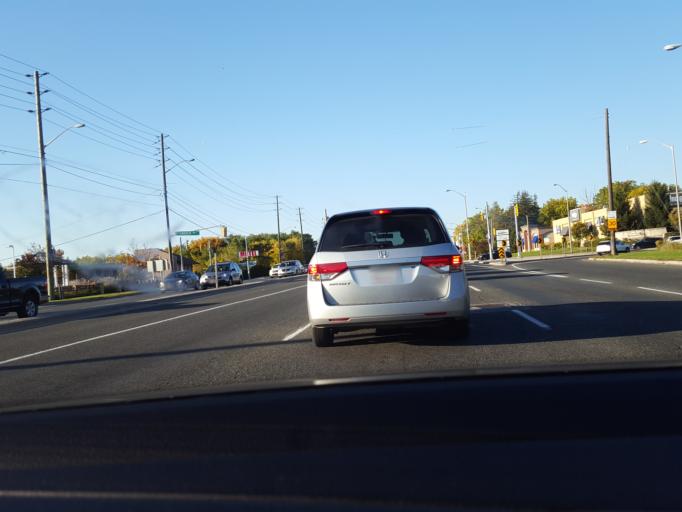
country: CA
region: Ontario
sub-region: York
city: Richmond Hill
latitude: 43.8384
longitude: -79.4294
